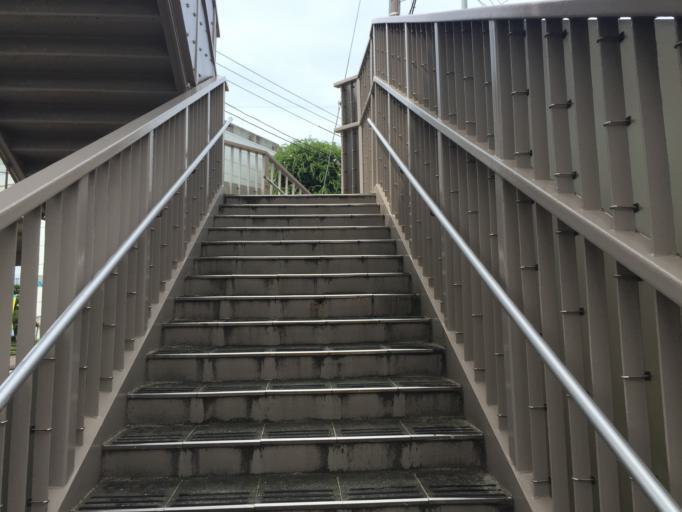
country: JP
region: Shizuoka
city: Numazu
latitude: 35.0964
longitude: 138.8634
